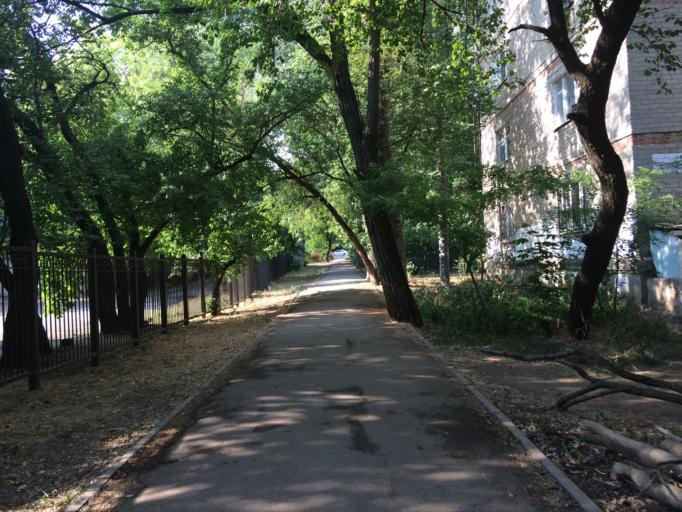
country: RU
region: Rostov
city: Rostov-na-Donu
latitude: 47.2113
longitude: 39.6421
